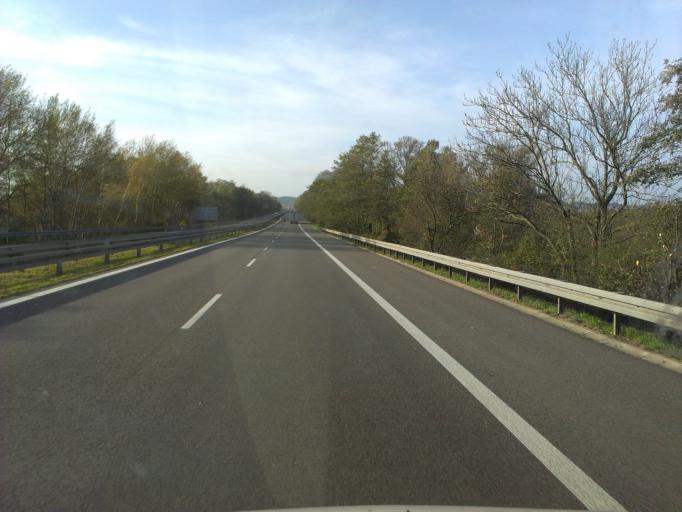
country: PL
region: West Pomeranian Voivodeship
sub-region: Powiat policki
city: Przeclaw
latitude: 53.3353
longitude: 14.5231
